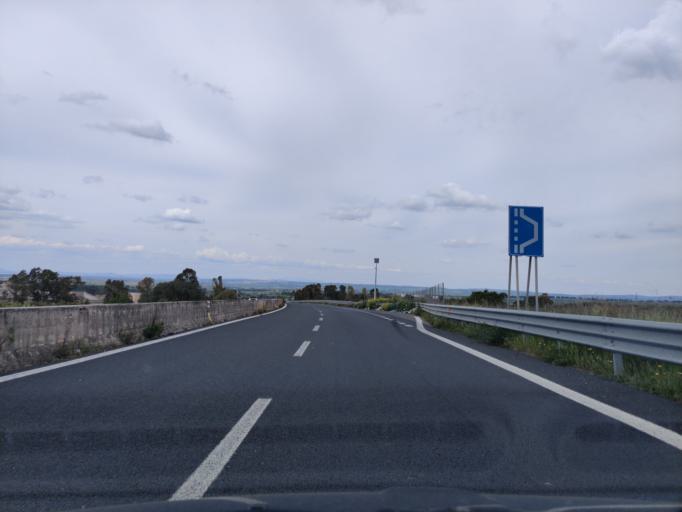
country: IT
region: Latium
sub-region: Citta metropolitana di Roma Capitale
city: Aurelia
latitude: 42.1372
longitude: 11.7951
